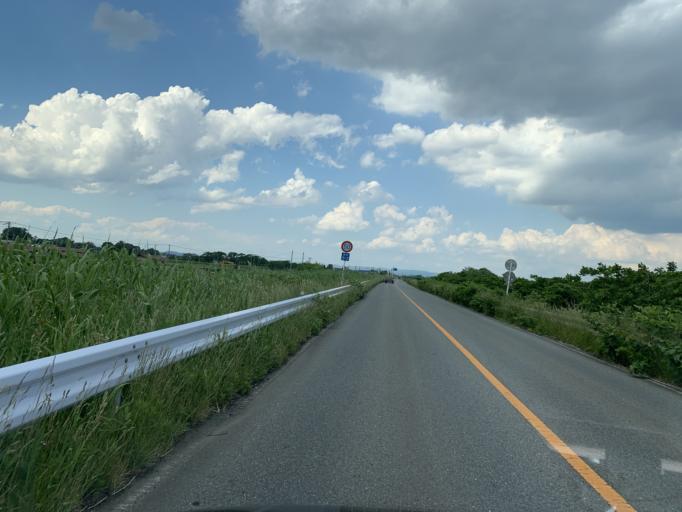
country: JP
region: Miyagi
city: Wakuya
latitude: 38.6401
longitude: 141.2060
